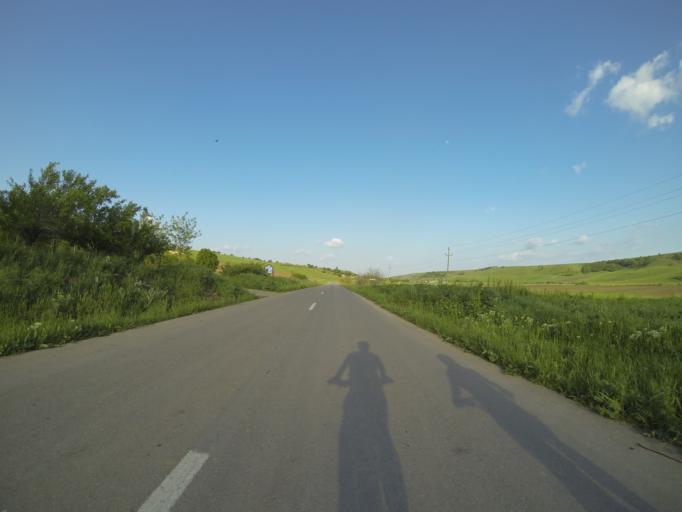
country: RO
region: Dolj
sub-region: Comuna Vela
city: Vela
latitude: 44.2689
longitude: 23.3721
